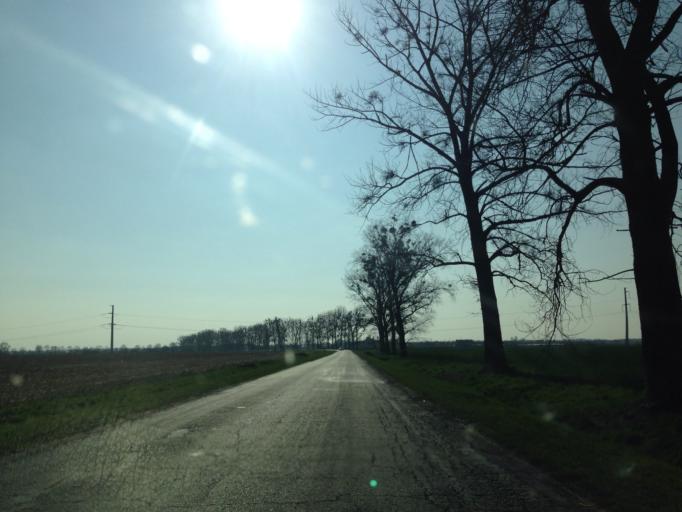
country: PL
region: Lower Silesian Voivodeship
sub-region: Powiat wroclawski
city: Kielczow
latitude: 51.1434
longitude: 17.2060
